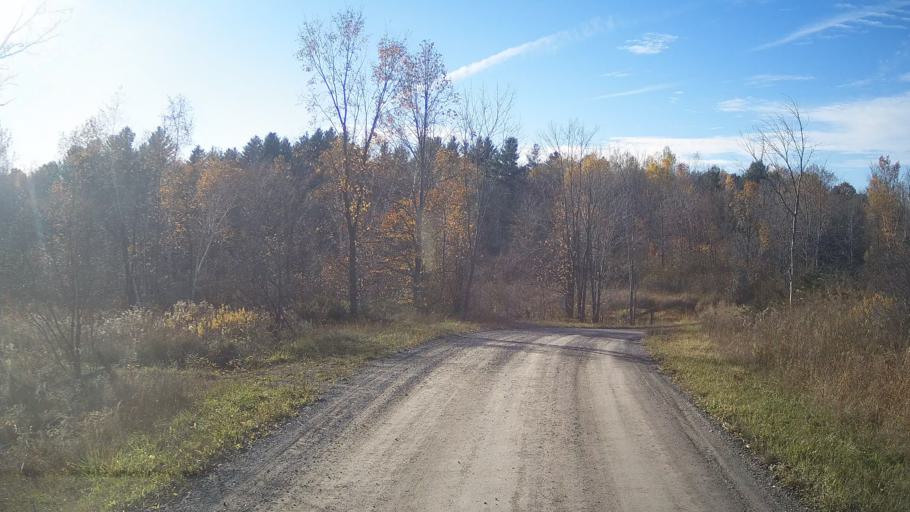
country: CA
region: Ontario
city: Perth
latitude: 44.7169
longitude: -76.4050
